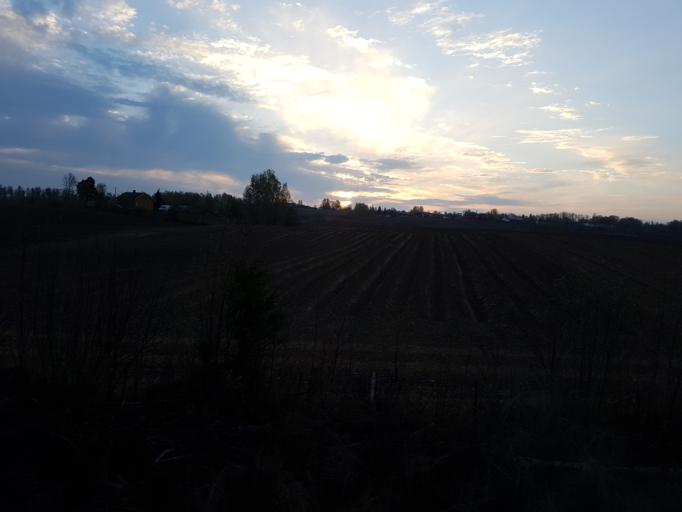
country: NO
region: Hedmark
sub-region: Hamar
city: Hamar
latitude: 60.7578
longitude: 11.1092
